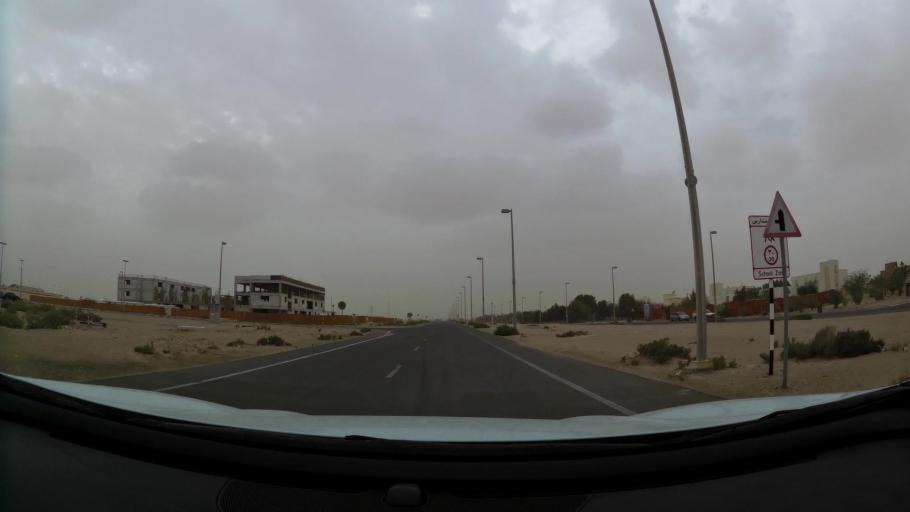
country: AE
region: Abu Dhabi
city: Abu Dhabi
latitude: 24.4254
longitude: 54.7274
